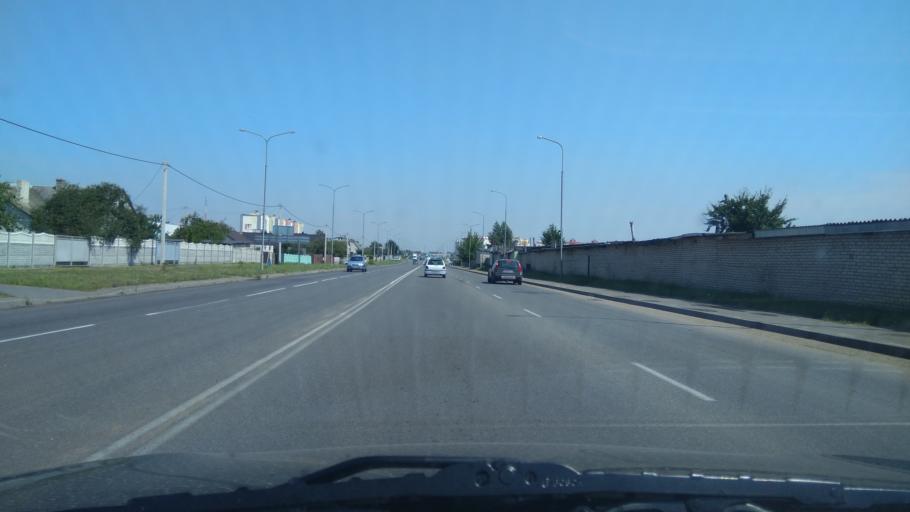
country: BY
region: Brest
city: Baranovichi
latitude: 53.1039
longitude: 25.9717
